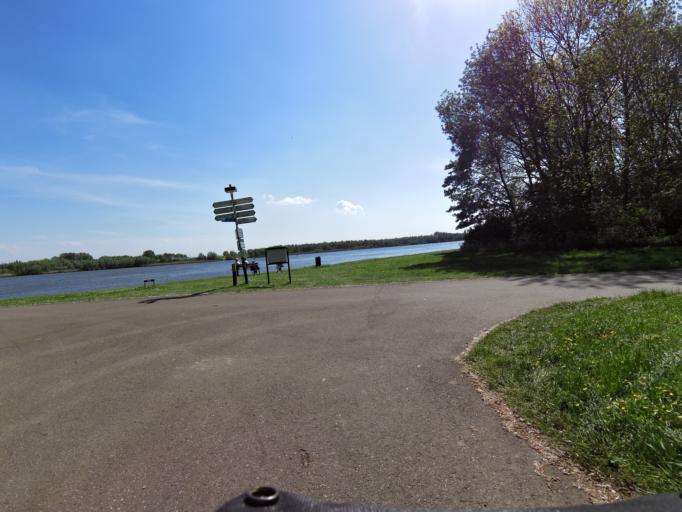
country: NL
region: South Holland
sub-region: Gemeente Binnenmaas
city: Heinenoord
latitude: 51.8343
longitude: 4.4678
